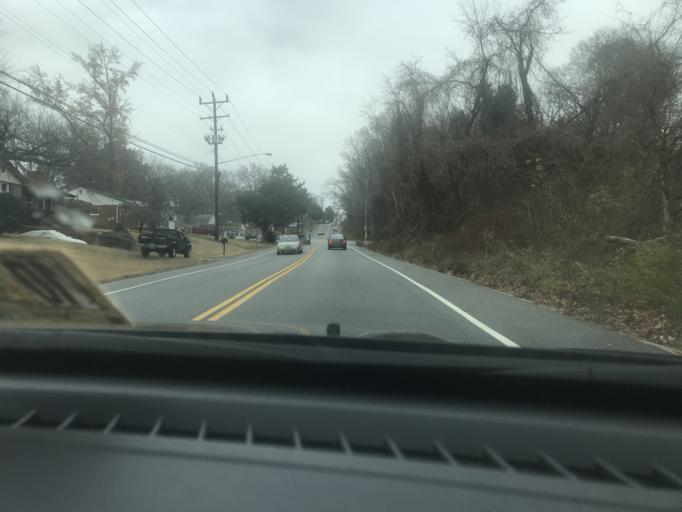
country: US
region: Maryland
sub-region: Prince George's County
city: Temple Hills
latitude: 38.8002
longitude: -76.9392
